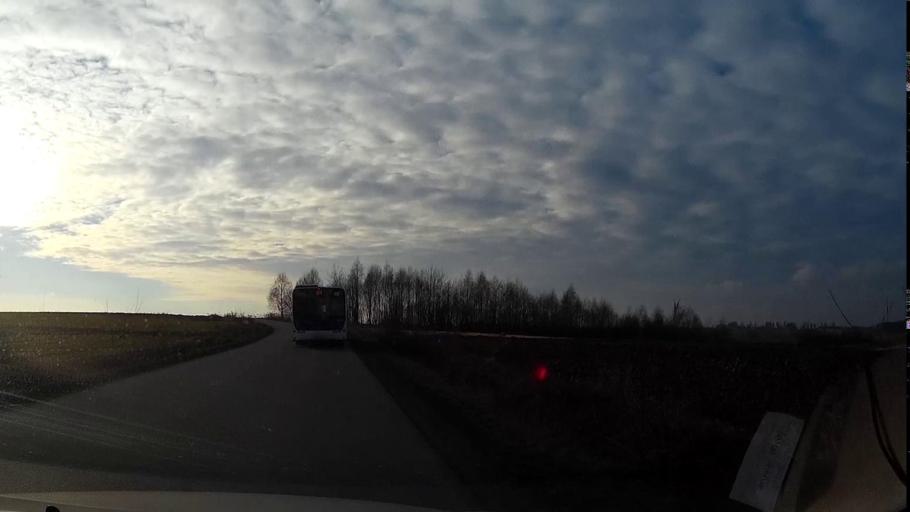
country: PL
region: Lesser Poland Voivodeship
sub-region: Powiat krakowski
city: Czulow
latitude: 50.0637
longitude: 19.6747
